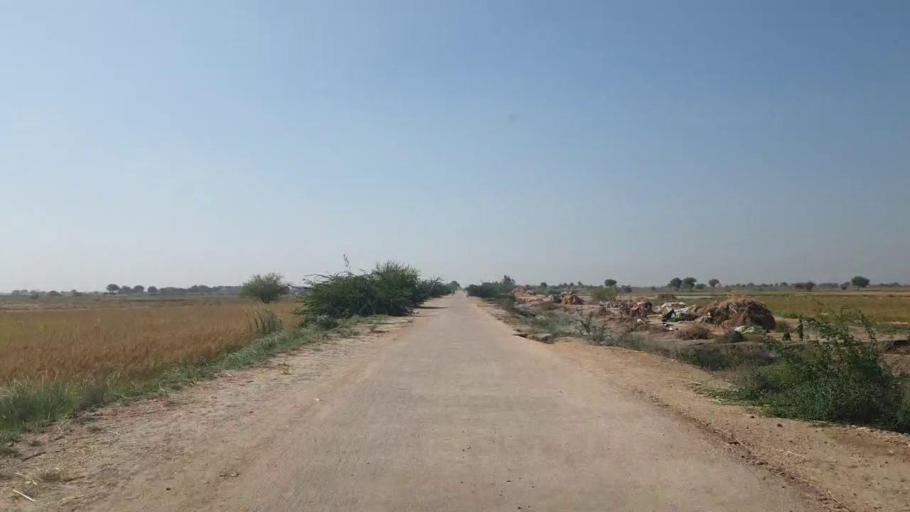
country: PK
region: Sindh
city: Talhar
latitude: 24.8244
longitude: 68.7675
